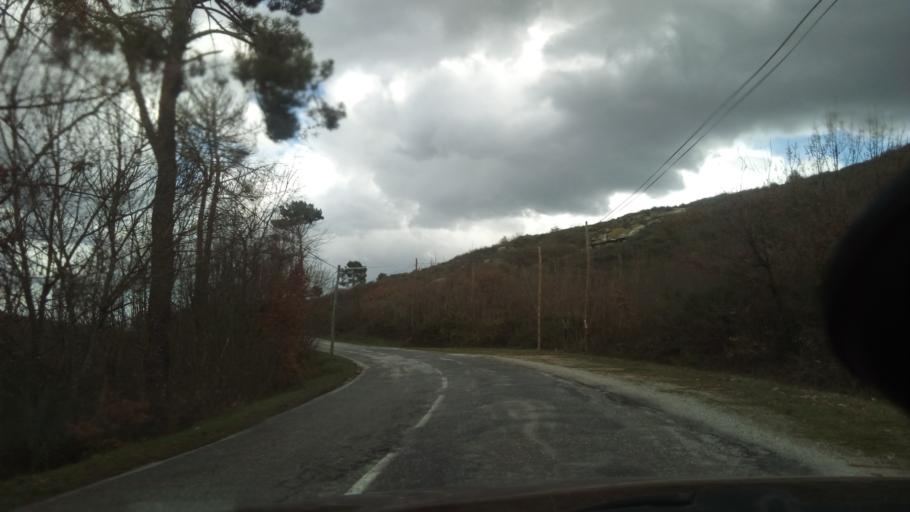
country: PT
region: Guarda
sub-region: Fornos de Algodres
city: Fornos de Algodres
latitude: 40.6273
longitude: -7.4655
